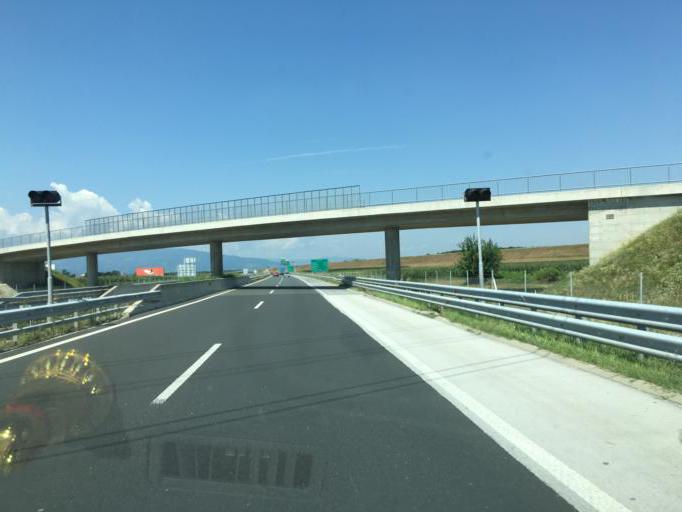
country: SI
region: Starse
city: Starse
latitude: 46.4454
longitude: 15.7746
